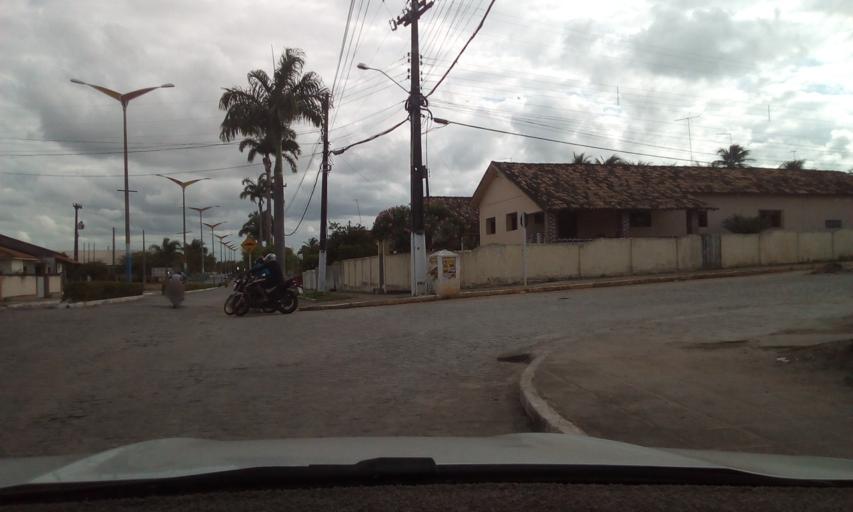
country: BR
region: Paraiba
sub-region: Rio Tinto
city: Rio Tinto
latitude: -6.8110
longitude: -35.0793
